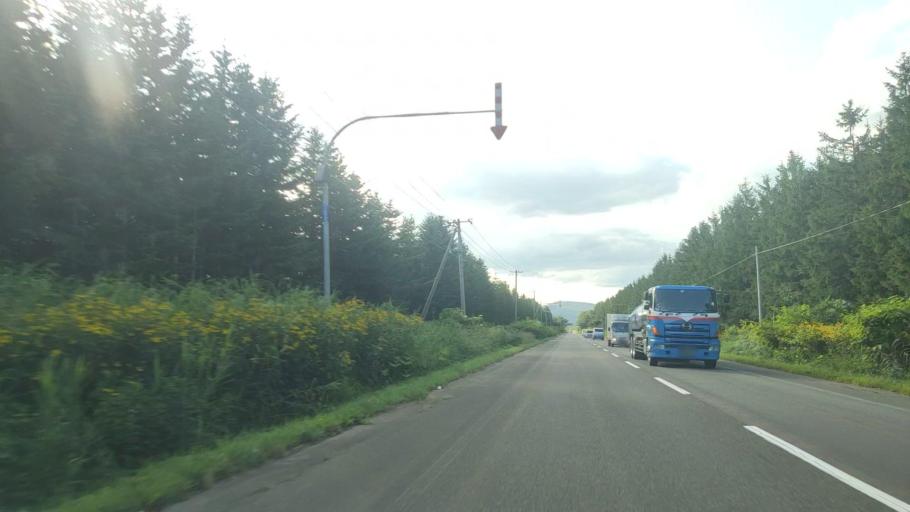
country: JP
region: Hokkaido
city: Makubetsu
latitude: 44.8879
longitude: 142.0062
